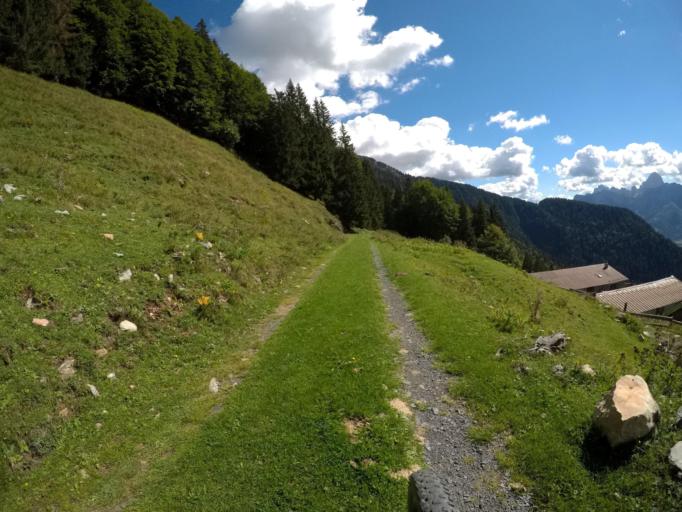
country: IT
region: Friuli Venezia Giulia
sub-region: Provincia di Udine
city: Paularo
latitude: 46.5670
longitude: 13.1223
